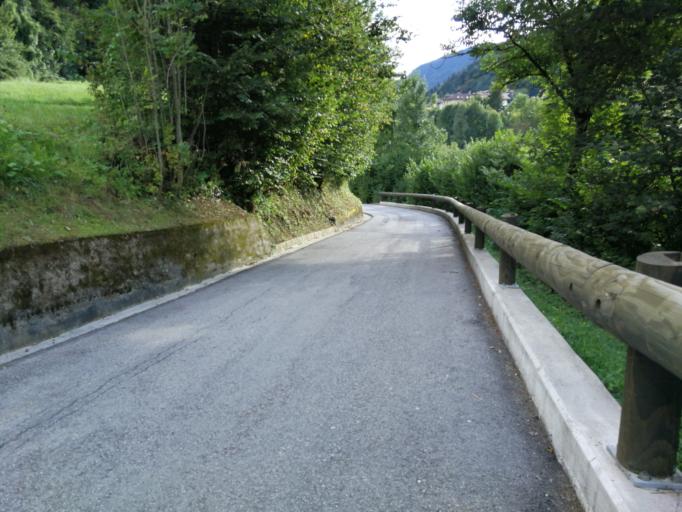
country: IT
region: Trentino-Alto Adige
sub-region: Provincia di Trento
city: Bondo
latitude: 46.0003
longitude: 10.6972
